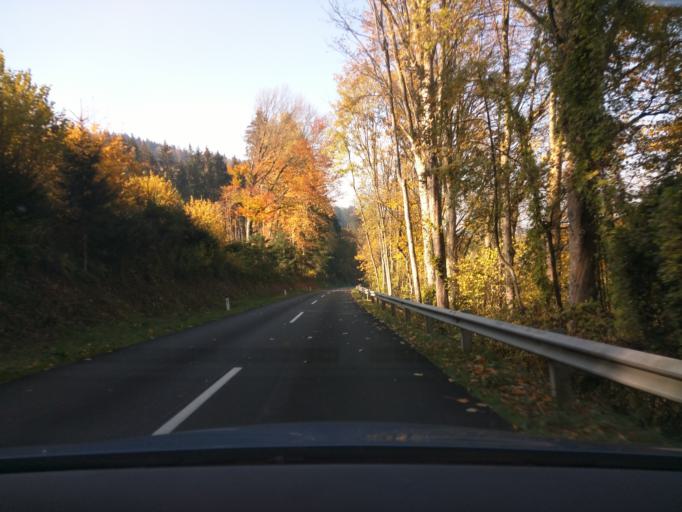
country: DE
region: Bavaria
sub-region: Lower Bavaria
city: Thyrnau
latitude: 48.5665
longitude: 13.5520
